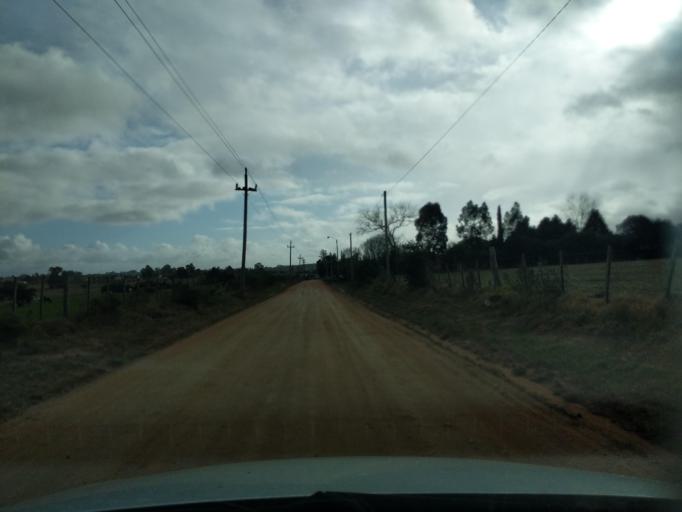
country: UY
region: Florida
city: Florida
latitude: -34.0711
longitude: -56.2206
